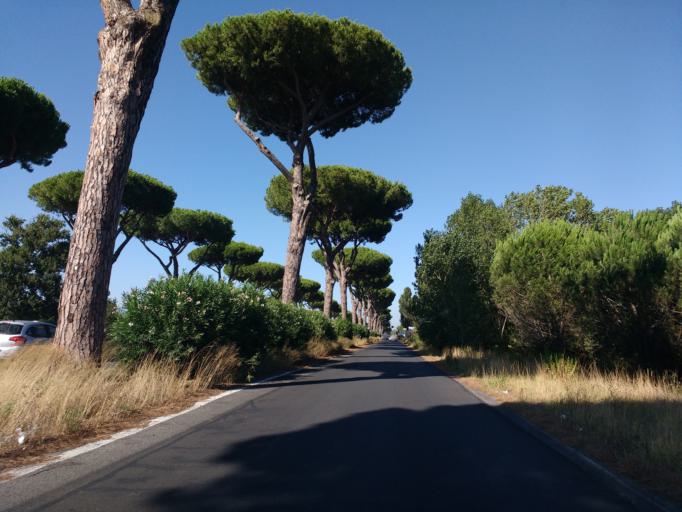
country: IT
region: Latium
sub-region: Citta metropolitana di Roma Capitale
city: Acilia-Castel Fusano-Ostia Antica
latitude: 41.7345
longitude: 12.3436
